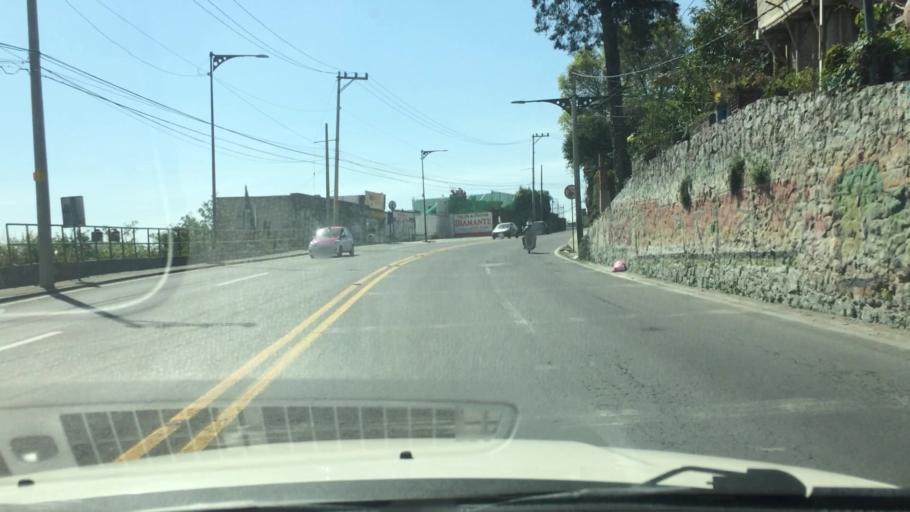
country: MX
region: Mexico City
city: Tlalpan
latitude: 19.2493
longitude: -99.1734
